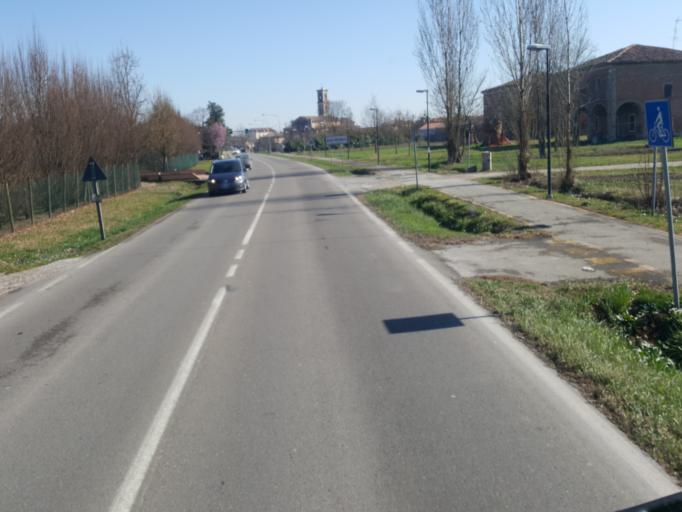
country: IT
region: Emilia-Romagna
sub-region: Provincia di Modena
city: Solara
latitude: 44.7710
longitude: 11.0715
